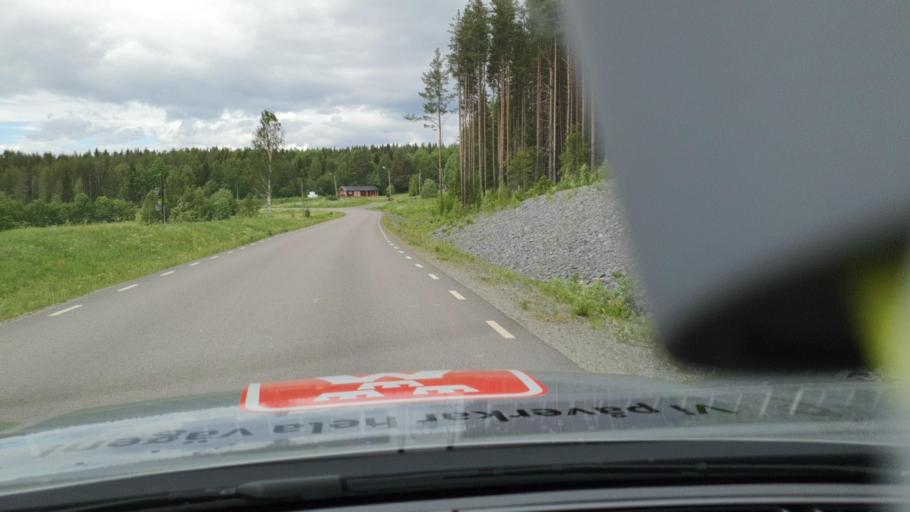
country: SE
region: Norrbotten
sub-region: Lulea Kommun
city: Sodra Sunderbyn
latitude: 65.8366
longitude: 21.9496
